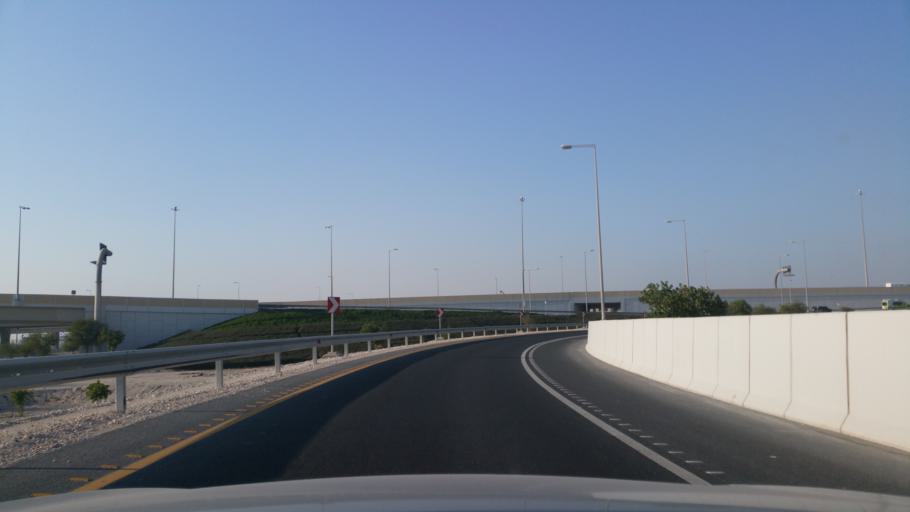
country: QA
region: Al Wakrah
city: Al Wukayr
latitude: 25.1611
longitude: 51.5693
